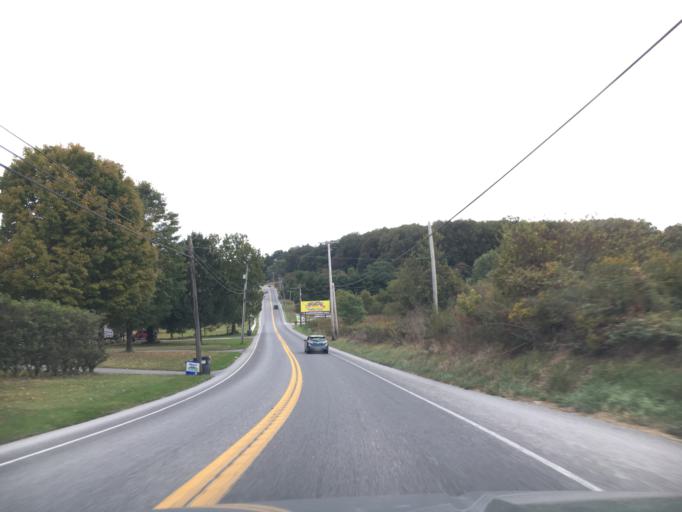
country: US
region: Pennsylvania
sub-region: Lancaster County
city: Quarryville
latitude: 39.8772
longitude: -76.2189
